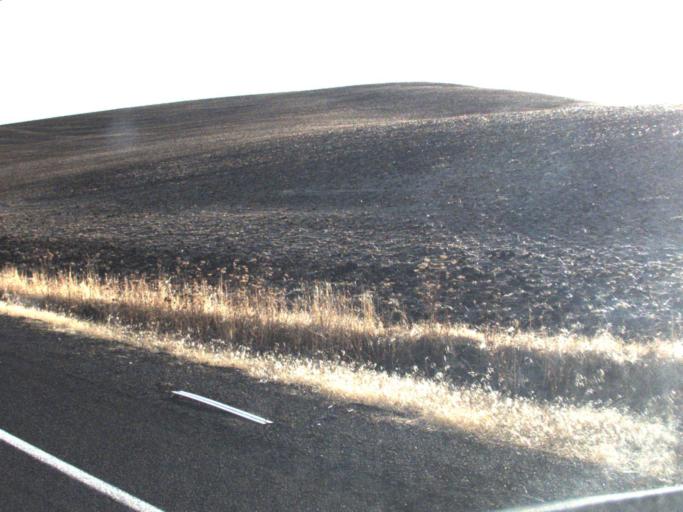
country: US
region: Washington
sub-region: Walla Walla County
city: Waitsburg
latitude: 46.1696
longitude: -118.1324
